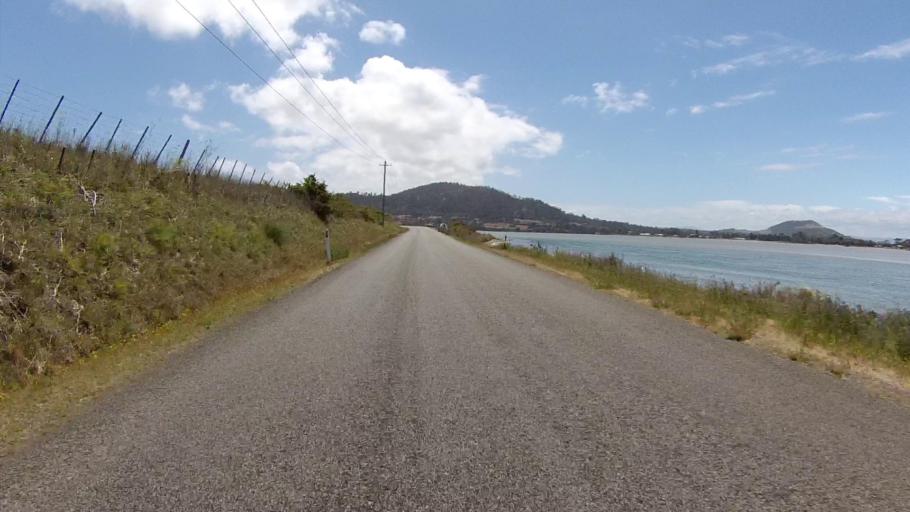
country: AU
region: Tasmania
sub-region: Clarence
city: Lauderdale
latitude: -42.9219
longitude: 147.4804
